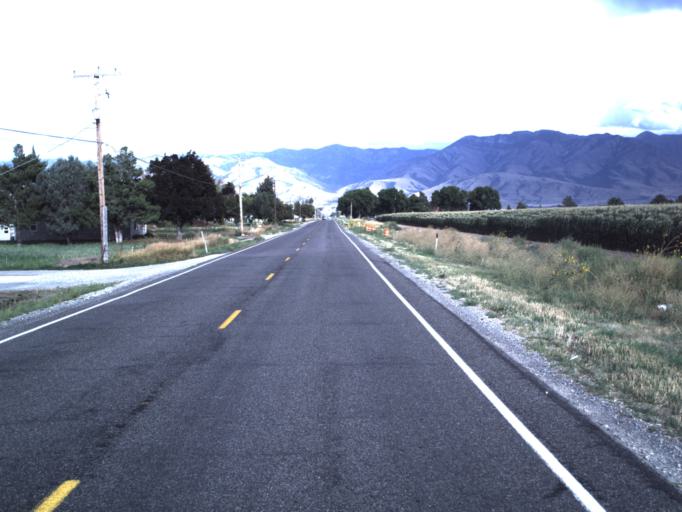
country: US
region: Utah
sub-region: Cache County
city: Lewiston
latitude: 41.9755
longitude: -111.9029
